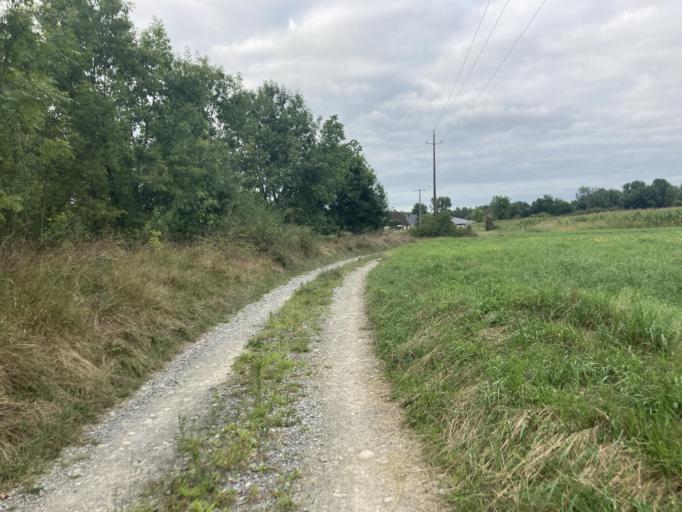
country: FR
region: Aquitaine
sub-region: Departement des Pyrenees-Atlantiques
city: Arbus
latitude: 43.3275
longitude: -0.4847
